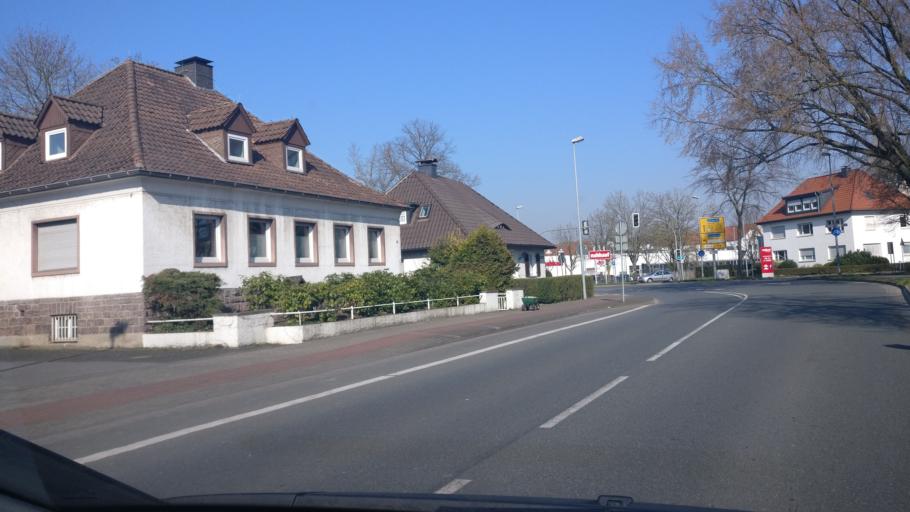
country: DE
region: North Rhine-Westphalia
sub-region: Regierungsbezirk Detmold
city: Lage
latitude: 51.9889
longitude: 8.7927
